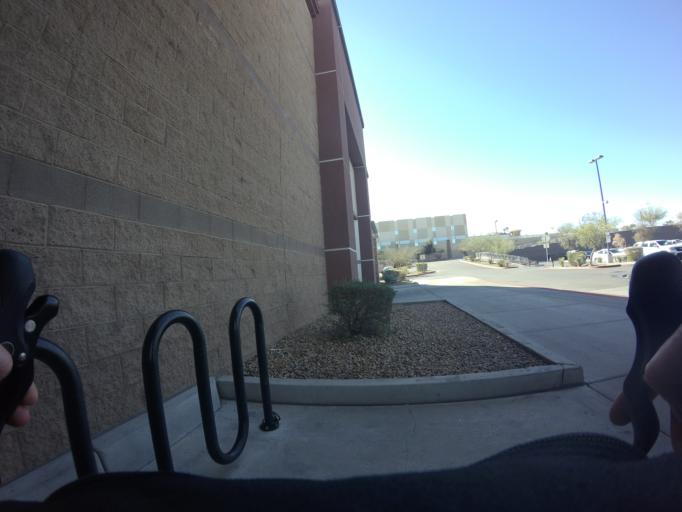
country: US
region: Nevada
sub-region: Clark County
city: Whitney
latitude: 36.0335
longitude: -115.0442
